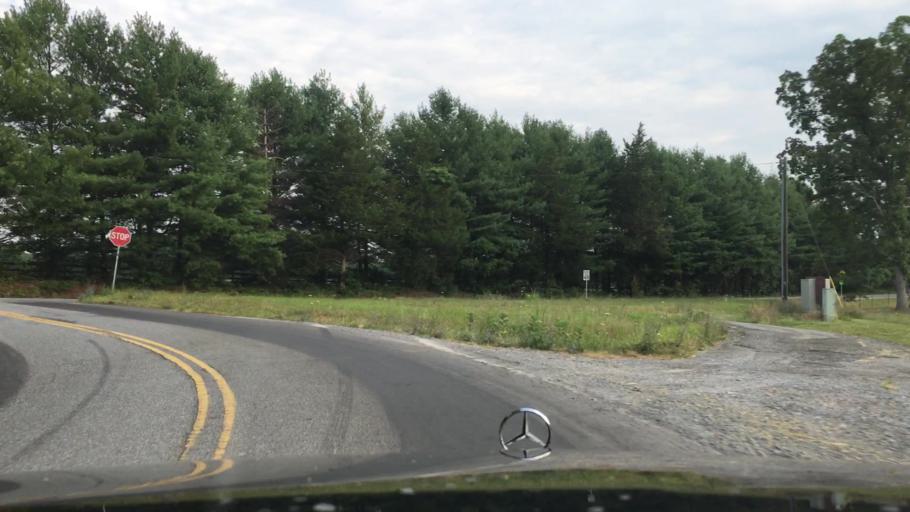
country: US
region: Virginia
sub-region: Campbell County
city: Timberlake
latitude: 37.2851
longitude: -79.3196
